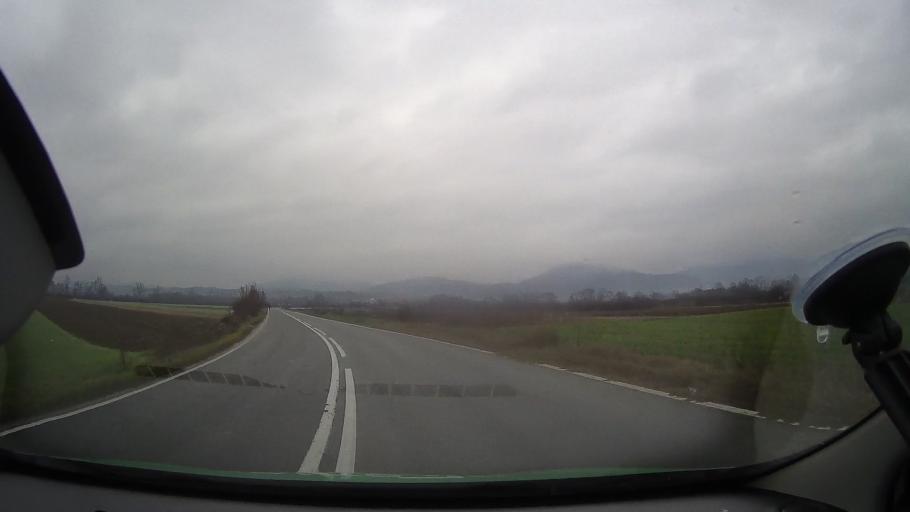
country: RO
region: Arad
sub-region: Comuna Gurahont
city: Gurahont
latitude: 46.2710
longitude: 22.3185
